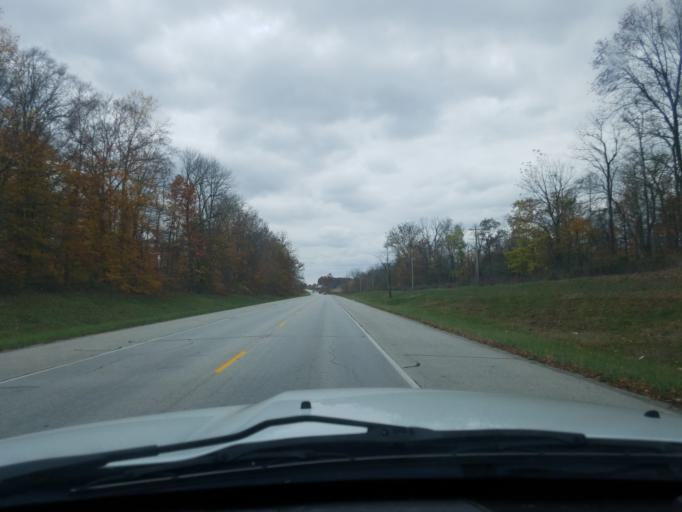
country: US
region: Indiana
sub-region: Bartholomew County
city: Columbus
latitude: 39.1732
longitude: -85.8182
